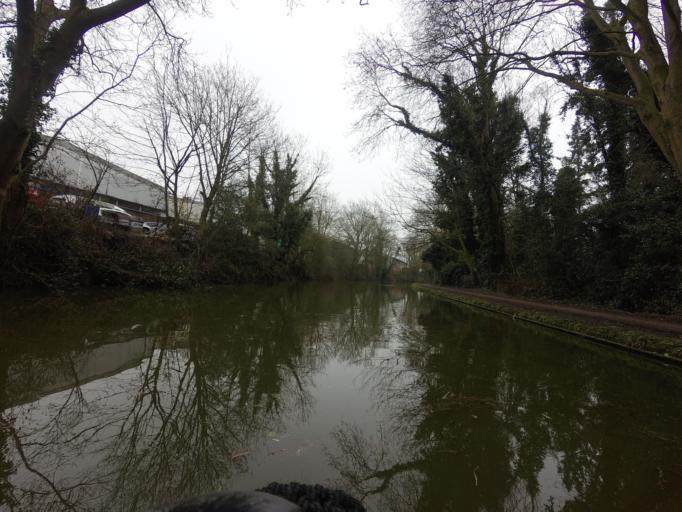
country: GB
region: England
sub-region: Hertfordshire
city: Berkhamsted
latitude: 51.7675
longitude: -0.5811
